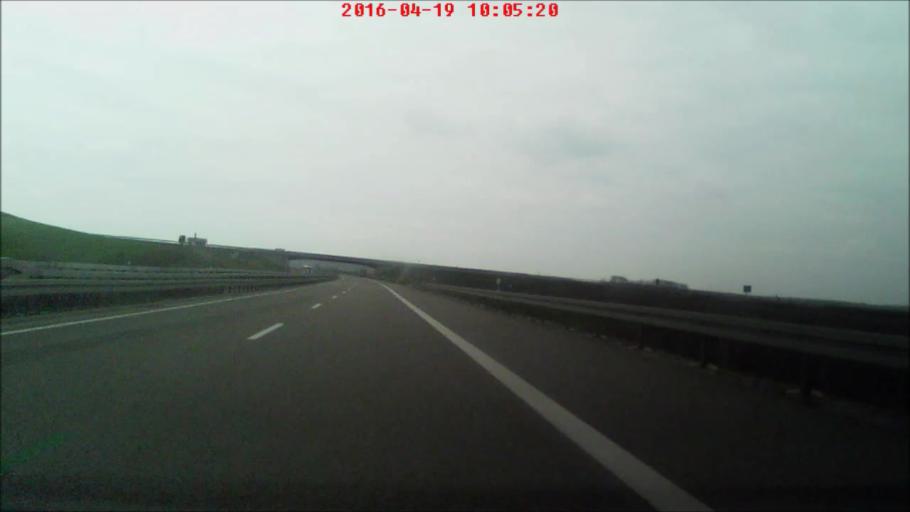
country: DE
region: Thuringia
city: Schillingstedt
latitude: 51.2406
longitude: 11.1846
